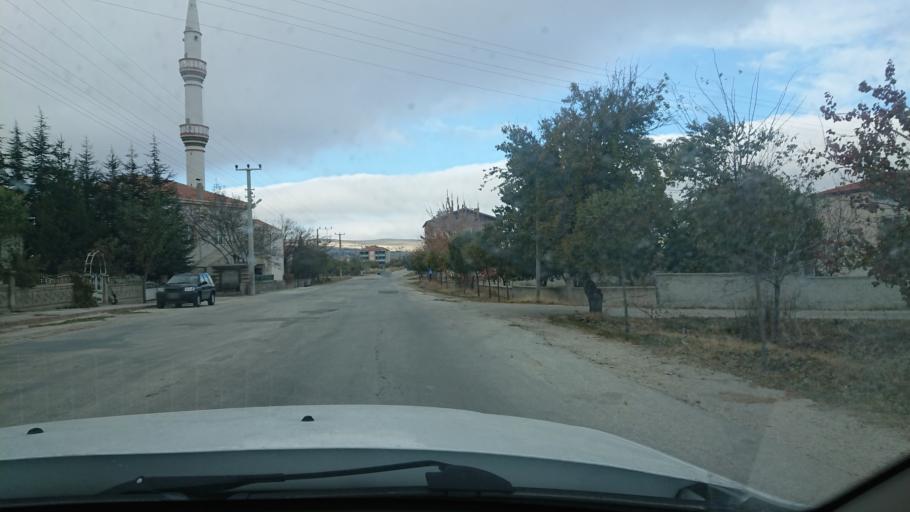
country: TR
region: Aksaray
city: Ortakoy
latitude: 38.7432
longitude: 34.0324
